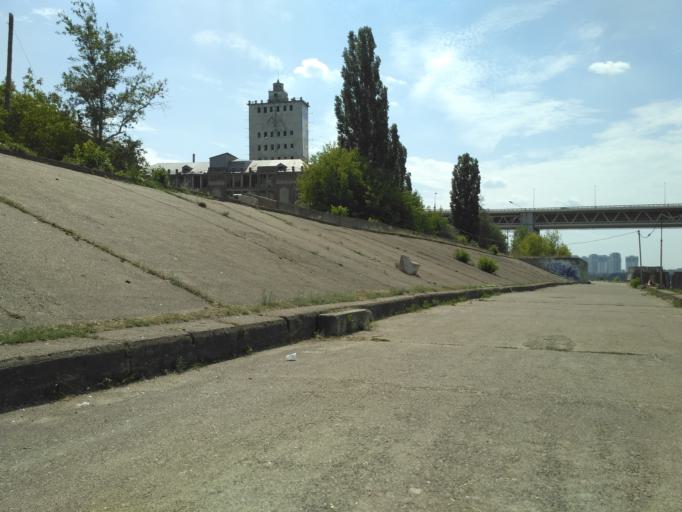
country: RU
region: Nizjnij Novgorod
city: Nizhniy Novgorod
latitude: 56.3200
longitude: 43.9717
